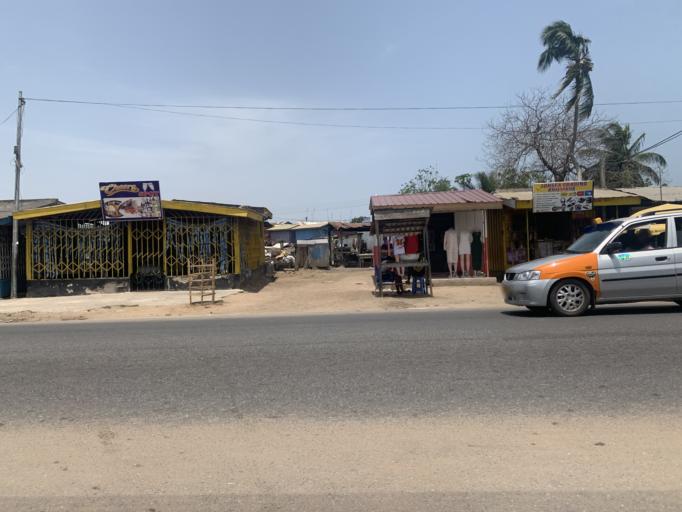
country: GH
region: Central
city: Winneba
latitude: 5.3484
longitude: -0.6294
